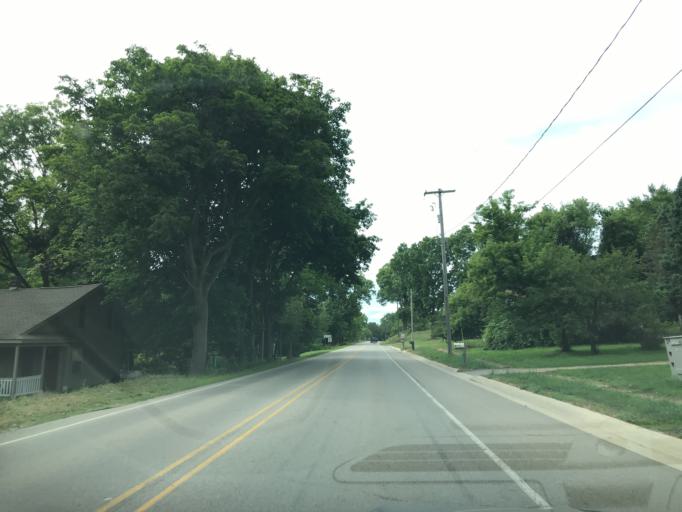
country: US
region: Michigan
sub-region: Jackson County
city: Spring Arbor
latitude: 42.0511
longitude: -84.5094
